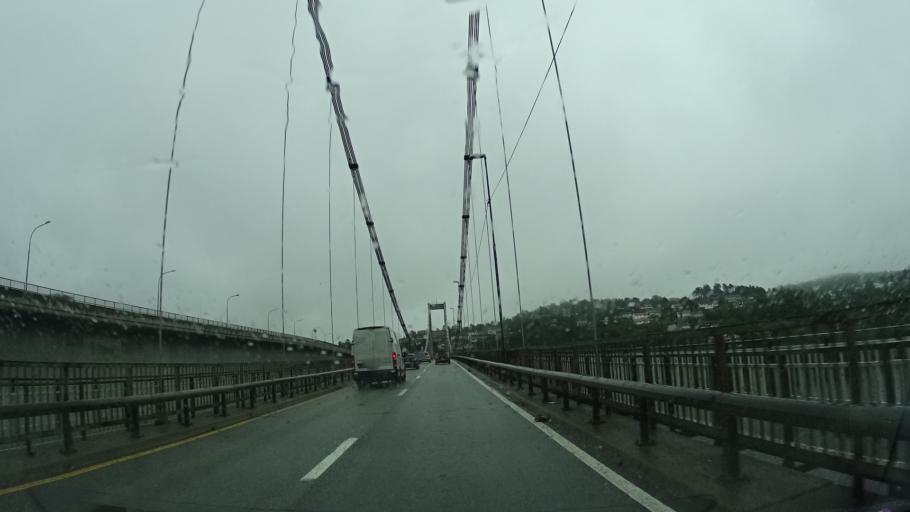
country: NO
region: Vest-Agder
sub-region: Kristiansand
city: Justvik
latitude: 58.1614
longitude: 8.0542
